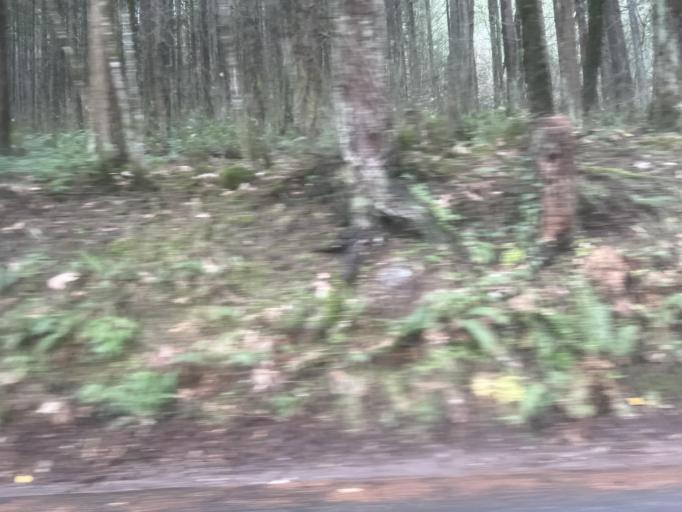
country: US
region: Washington
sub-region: Clark County
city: Washougal
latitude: 45.5506
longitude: -122.1887
